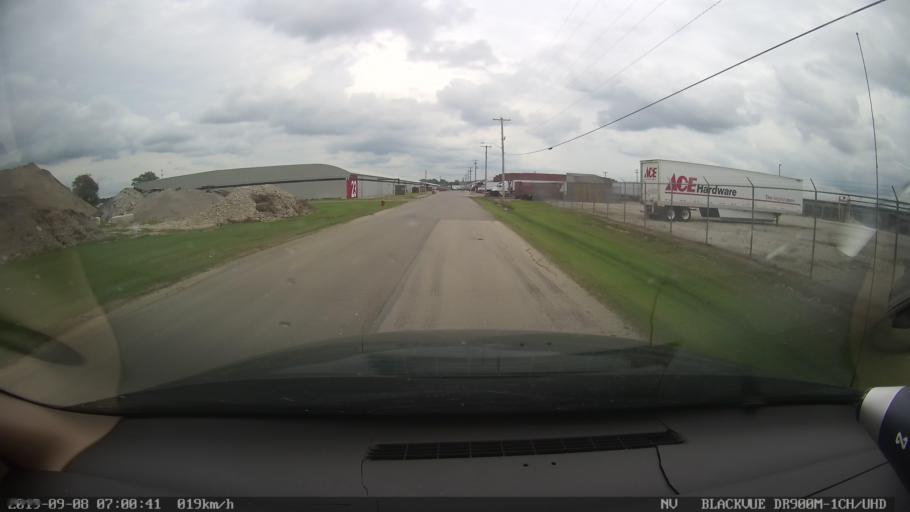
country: US
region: Ohio
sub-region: Richland County
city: Shelby
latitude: 40.9009
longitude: -82.6758
